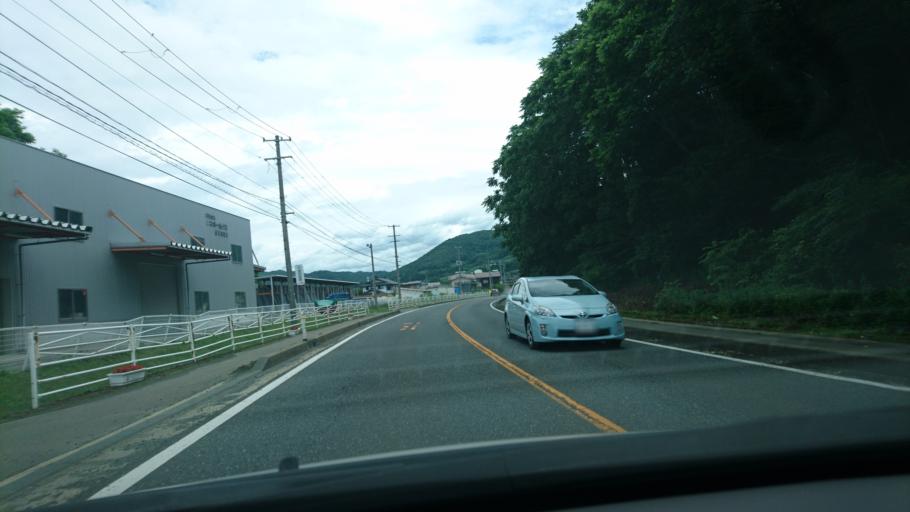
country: JP
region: Iwate
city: Morioka-shi
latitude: 39.6349
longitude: 141.1844
